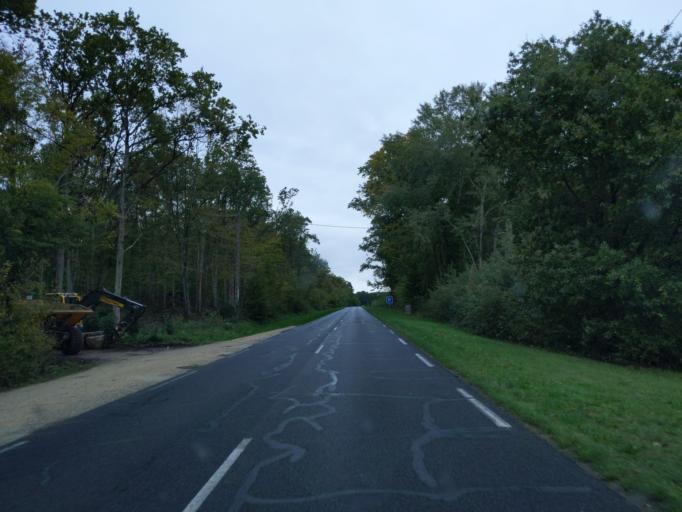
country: FR
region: Ile-de-France
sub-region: Departement des Yvelines
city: Saint-Arnoult-en-Yvelines
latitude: 48.5767
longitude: 1.9609
